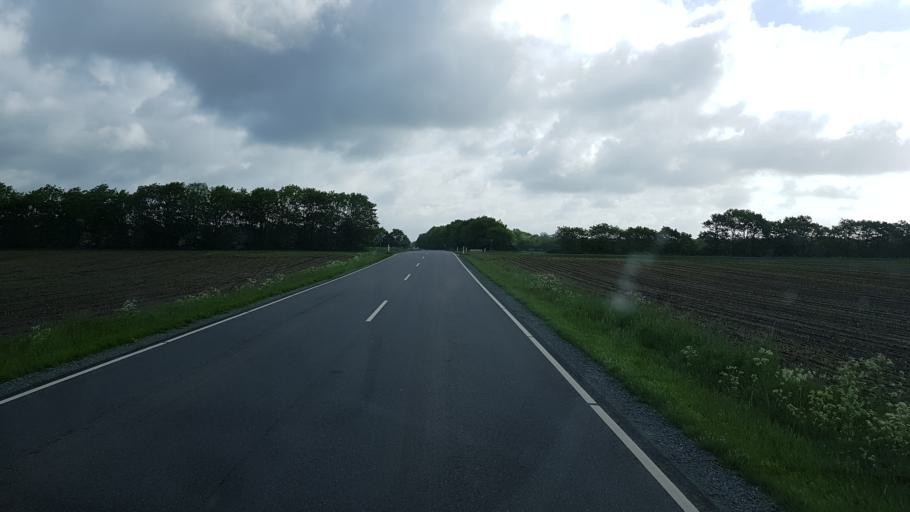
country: DK
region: South Denmark
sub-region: Vejen Kommune
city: Vejen
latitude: 55.4579
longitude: 9.1625
